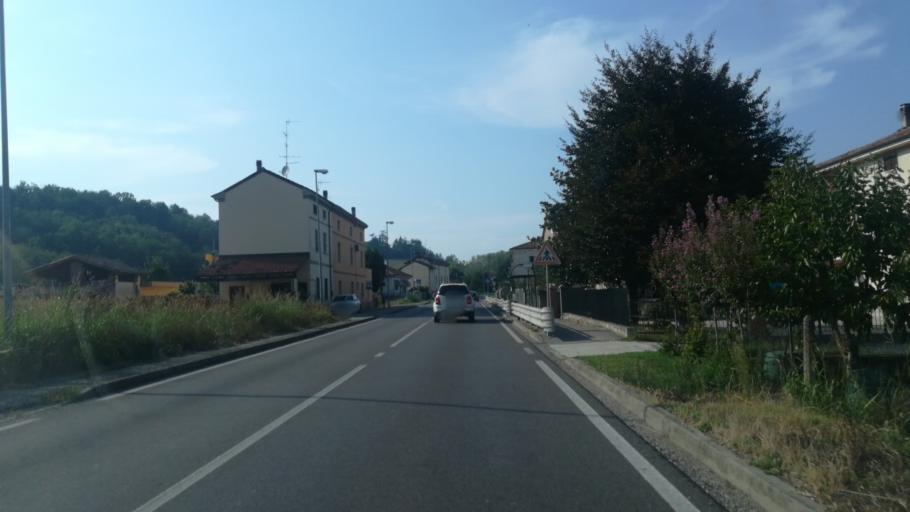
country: IT
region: Piedmont
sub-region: Provincia di Alessandria
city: Terruggia
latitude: 45.0891
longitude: 8.4653
